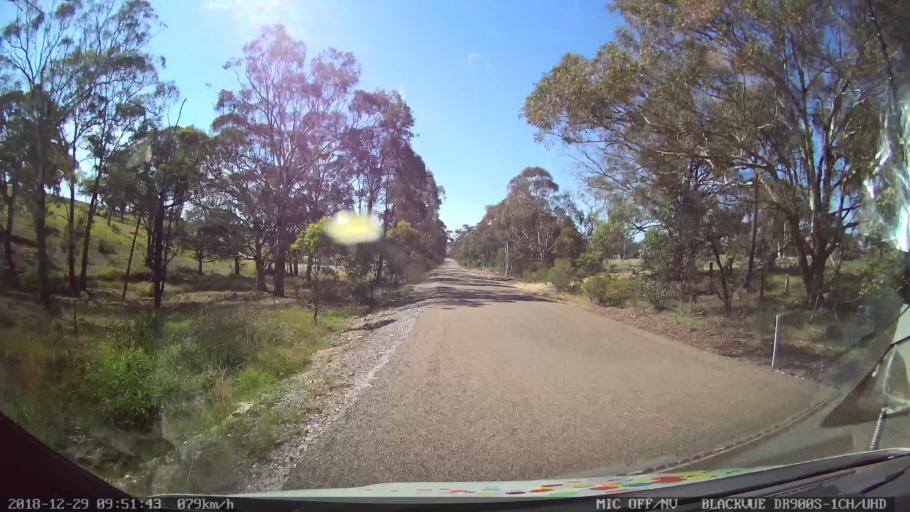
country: AU
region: New South Wales
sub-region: Goulburn Mulwaree
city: Goulburn
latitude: -34.7353
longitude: 149.4614
